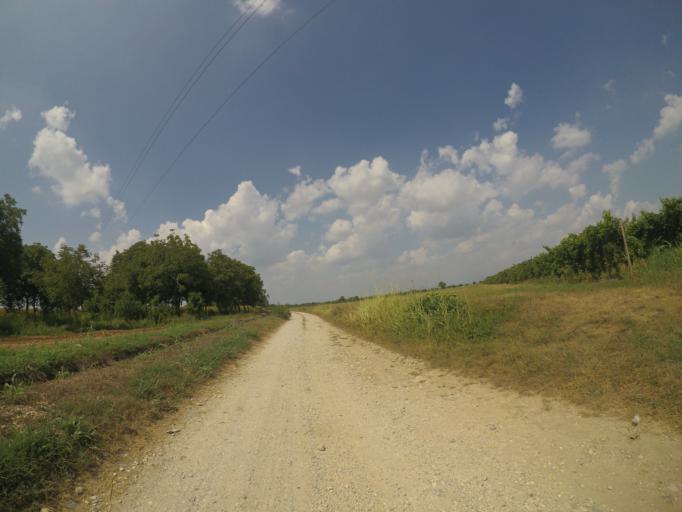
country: IT
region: Friuli Venezia Giulia
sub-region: Provincia di Udine
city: Bertiolo
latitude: 45.9502
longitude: 13.0374
